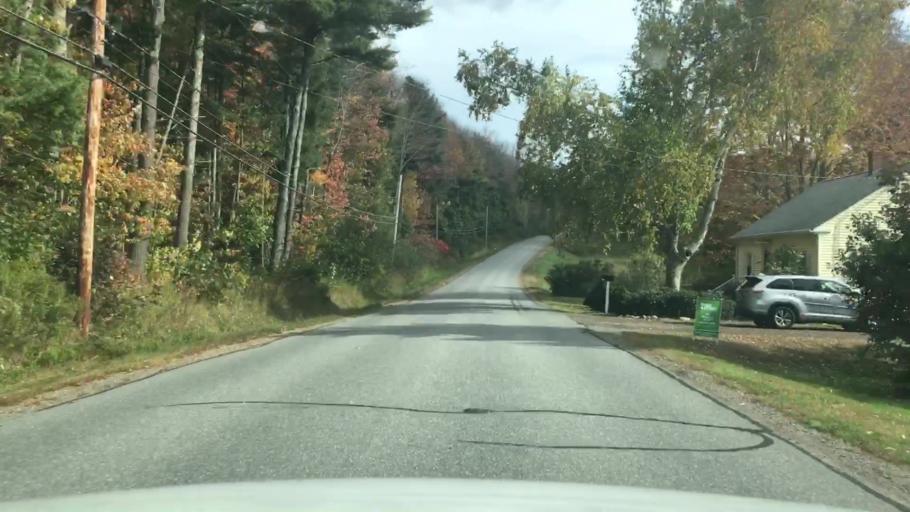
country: US
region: Maine
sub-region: Knox County
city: Rockport
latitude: 44.2047
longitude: -69.0910
